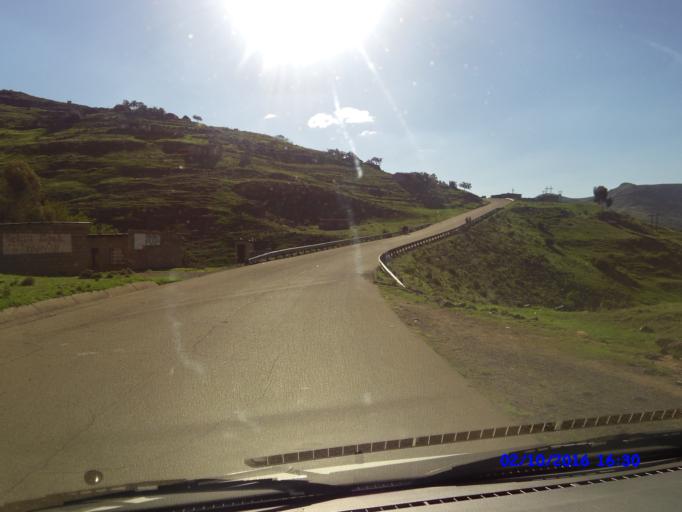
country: LS
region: Maseru
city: Nako
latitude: -29.4815
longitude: 28.0777
